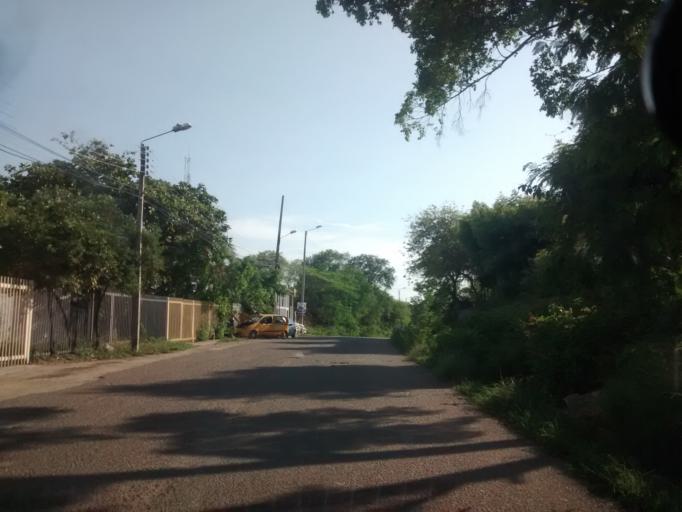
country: CO
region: Cundinamarca
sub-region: Girardot
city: Girardot City
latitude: 4.3259
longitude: -74.8037
